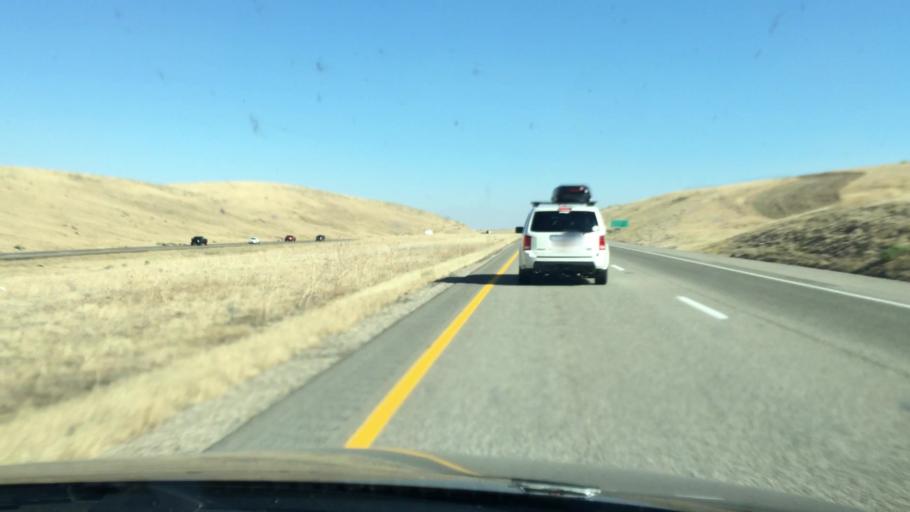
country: US
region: Idaho
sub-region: Ada County
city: Boise
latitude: 43.4994
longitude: -116.1352
